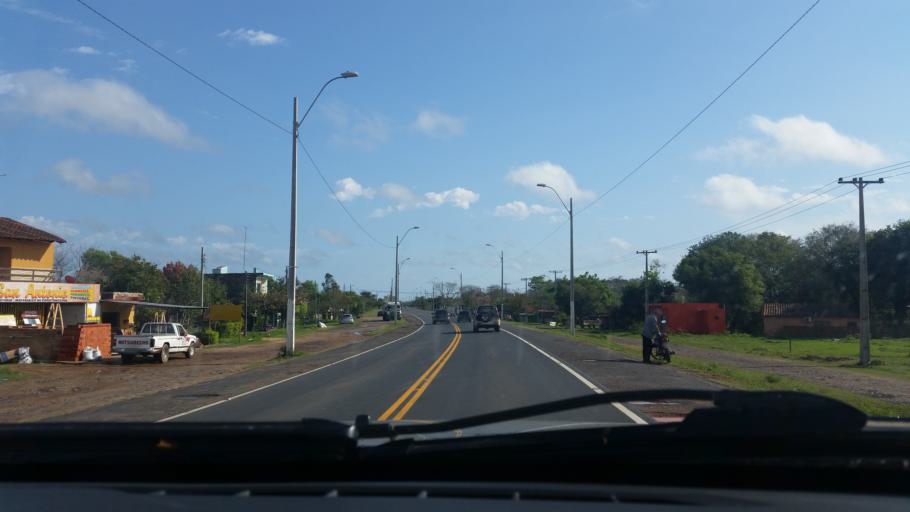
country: PY
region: Presidente Hayes
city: Benjamin Aceval
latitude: -24.9592
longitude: -57.5482
